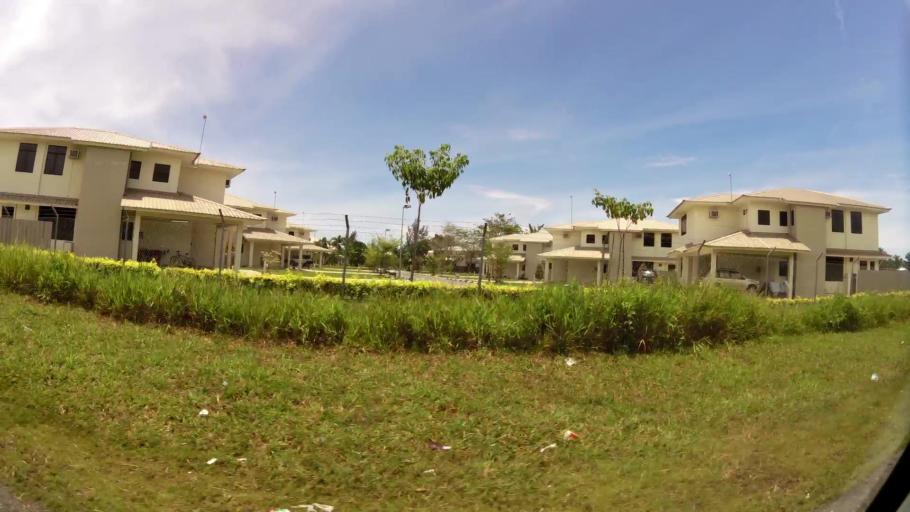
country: BN
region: Belait
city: Kuala Belait
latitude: 4.5895
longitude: 114.2494
